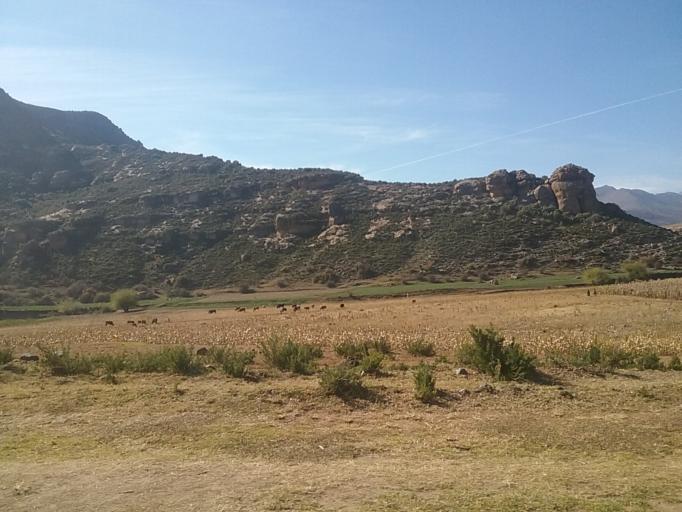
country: LS
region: Berea
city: Teyateyaneng
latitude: -29.2510
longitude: 27.9182
